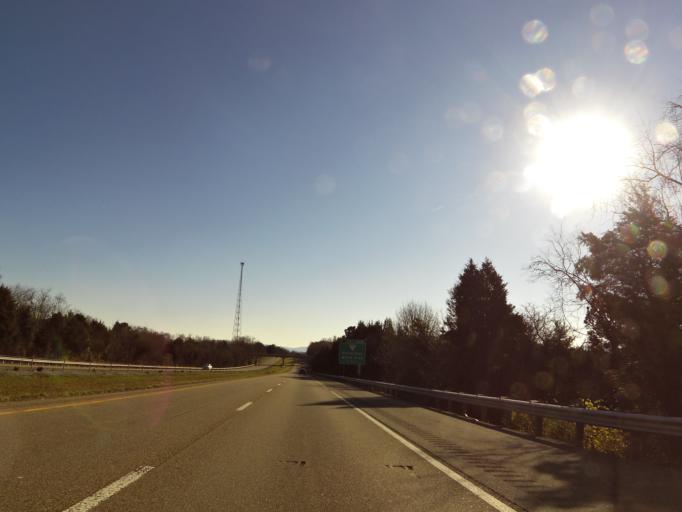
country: US
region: Tennessee
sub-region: Jefferson County
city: Dandridge
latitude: 36.0543
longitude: -83.3621
